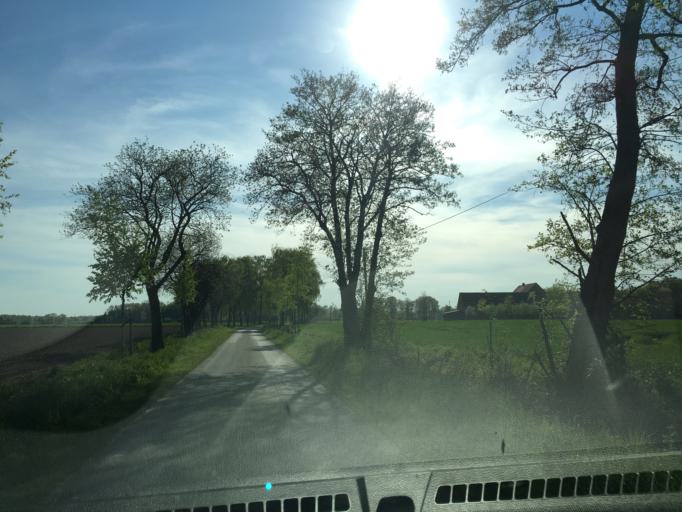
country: DE
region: North Rhine-Westphalia
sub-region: Regierungsbezirk Munster
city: Nordkirchen
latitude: 51.7545
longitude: 7.5031
